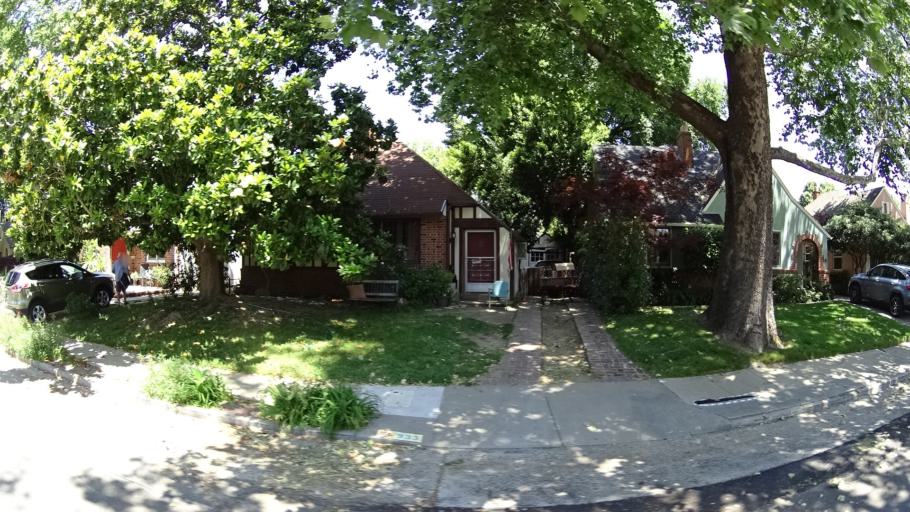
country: US
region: California
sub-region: Sacramento County
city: Sacramento
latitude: 38.5562
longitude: -121.5049
